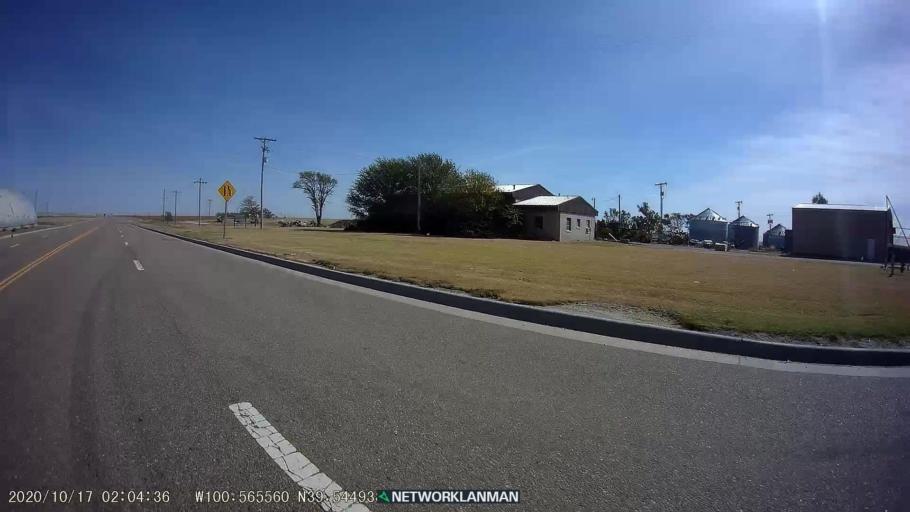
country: US
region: Kansas
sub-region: Sheridan County
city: Hoxie
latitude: 39.5451
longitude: -100.5651
